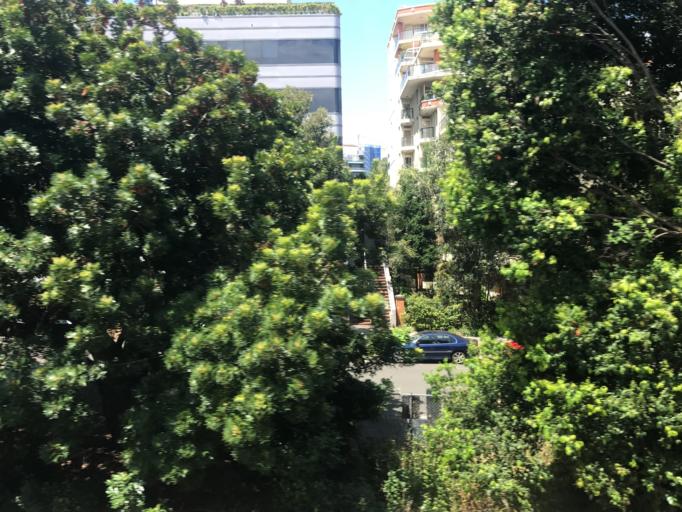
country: AU
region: New South Wales
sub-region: North Sydney
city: St Leonards
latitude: -33.8252
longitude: 151.1949
